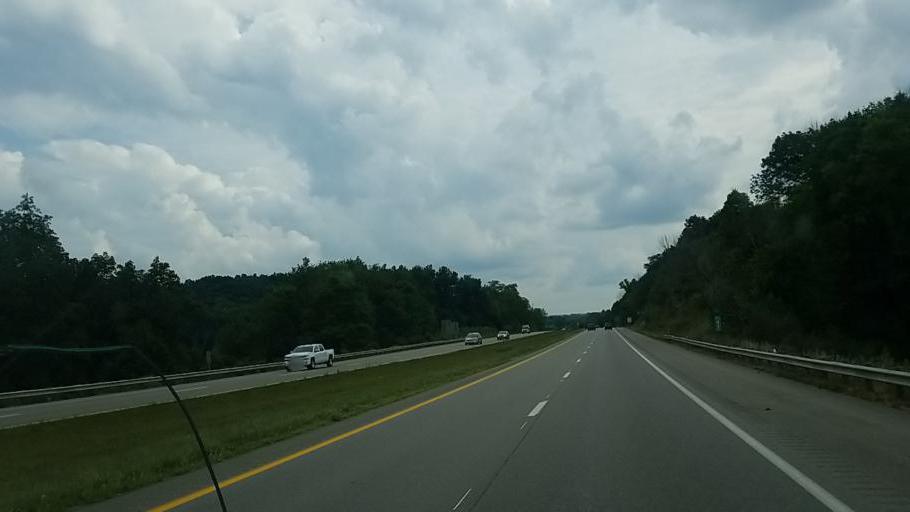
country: US
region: Ohio
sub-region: Guernsey County
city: Cambridge
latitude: 40.0400
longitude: -81.5613
